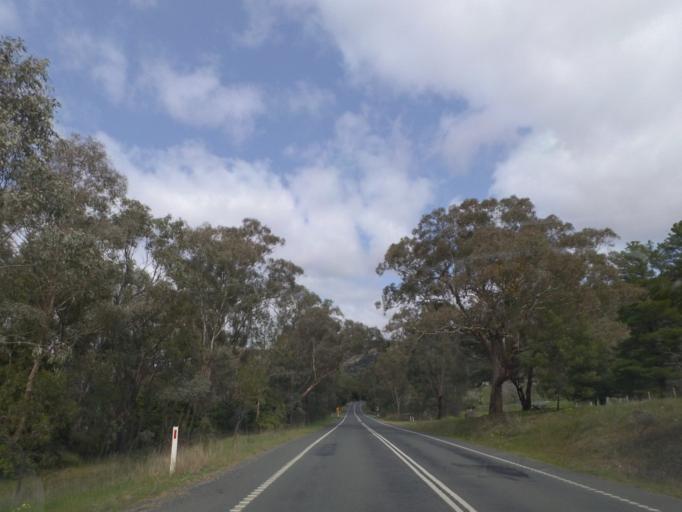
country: AU
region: Victoria
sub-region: Murrindindi
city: Kinglake West
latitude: -37.1043
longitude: 145.2082
